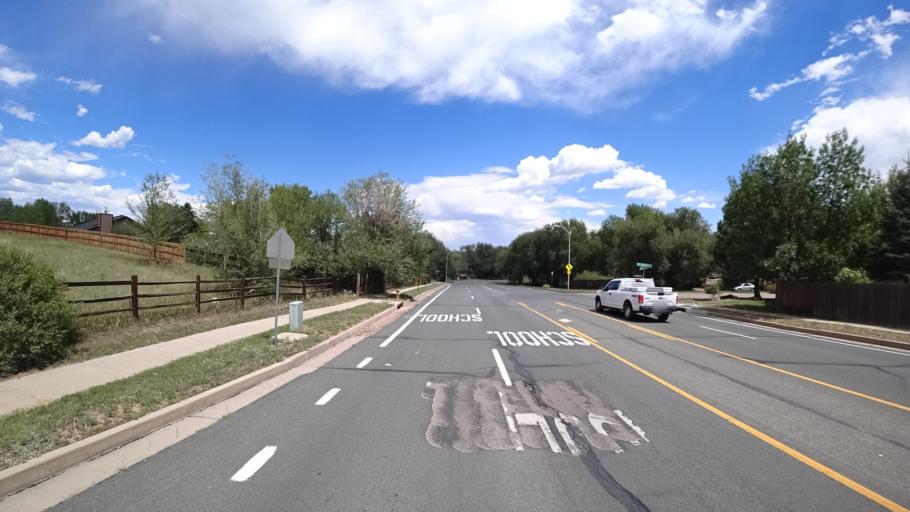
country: US
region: Colorado
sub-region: El Paso County
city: Stratmoor
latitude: 38.7834
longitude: -104.7995
